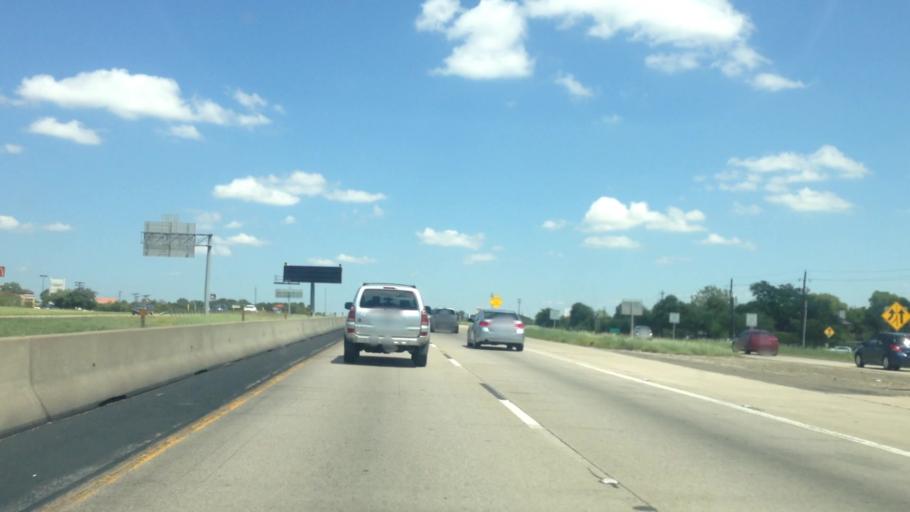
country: US
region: Texas
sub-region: Tarrant County
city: Bedford
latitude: 32.8482
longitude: -97.1132
